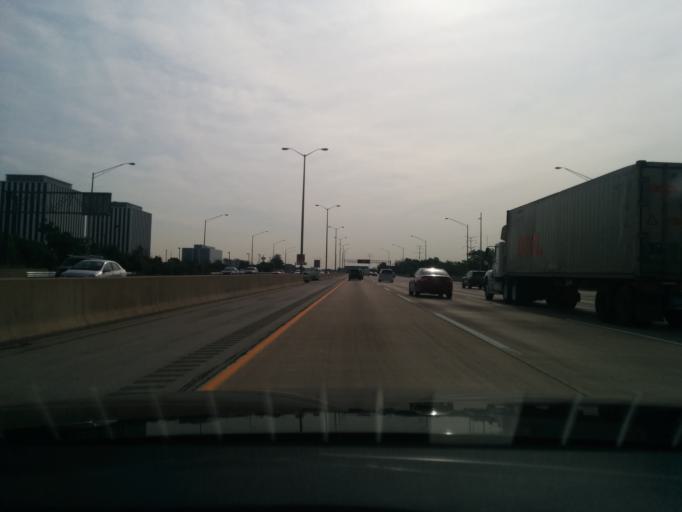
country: US
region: Illinois
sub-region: DuPage County
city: Oakbrook Terrace
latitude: 41.8446
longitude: -87.9544
